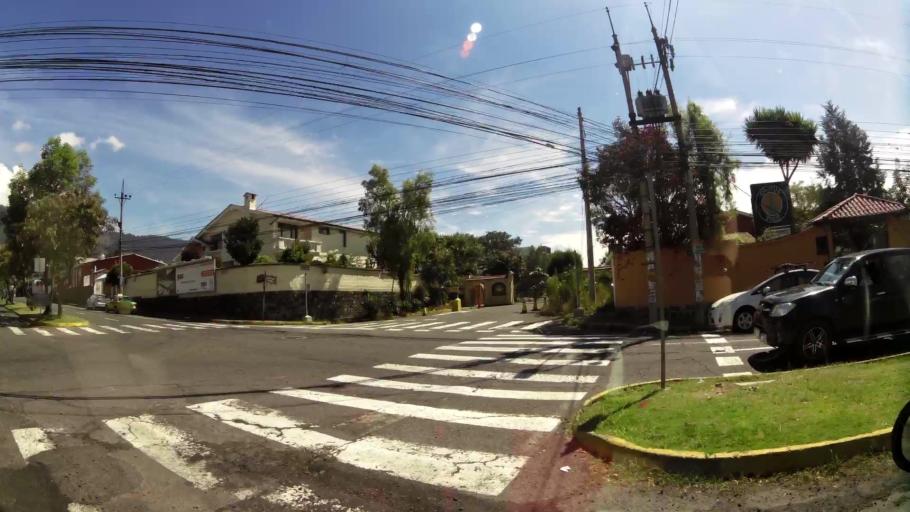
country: EC
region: Pichincha
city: Quito
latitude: -0.1953
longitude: -78.4360
